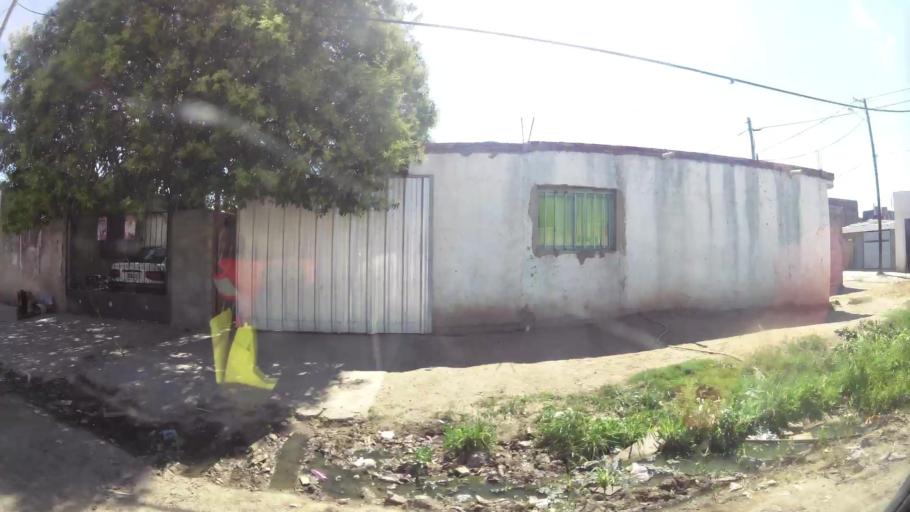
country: AR
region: Cordoba
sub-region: Departamento de Capital
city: Cordoba
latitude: -31.3669
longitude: -64.1422
